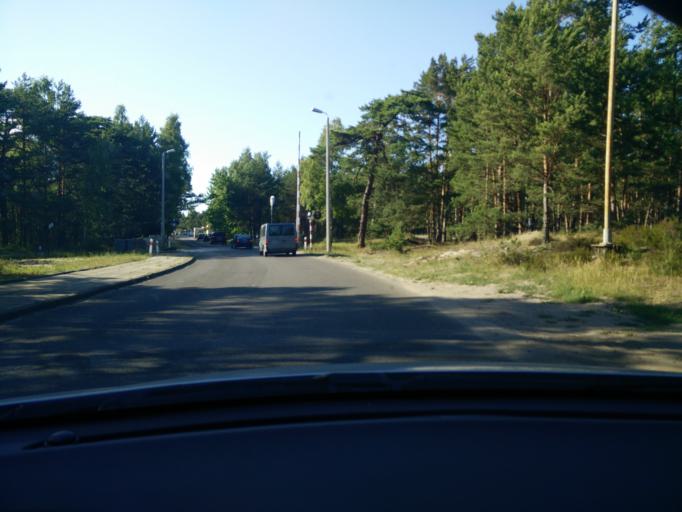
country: PL
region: Pomeranian Voivodeship
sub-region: Powiat pucki
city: Hel
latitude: 54.6172
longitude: 18.8036
